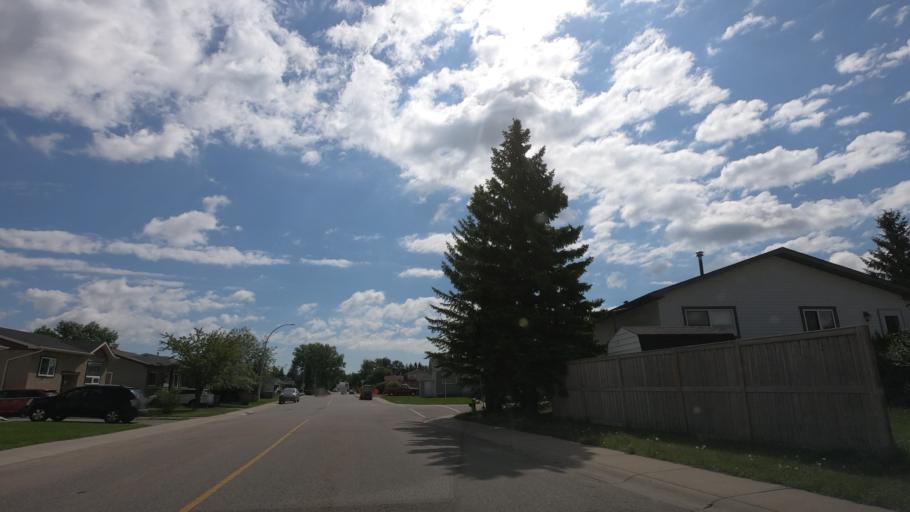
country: CA
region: Alberta
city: Airdrie
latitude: 51.2851
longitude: -114.0170
